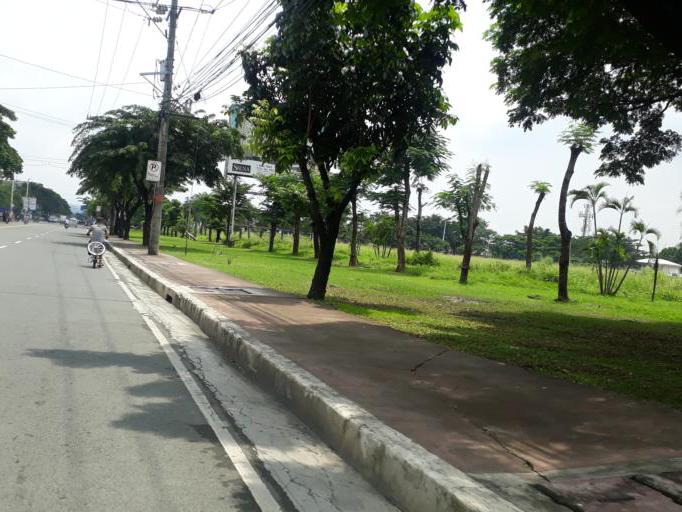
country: PH
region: Metro Manila
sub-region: Marikina
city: Calumpang
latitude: 14.6345
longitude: 121.1039
